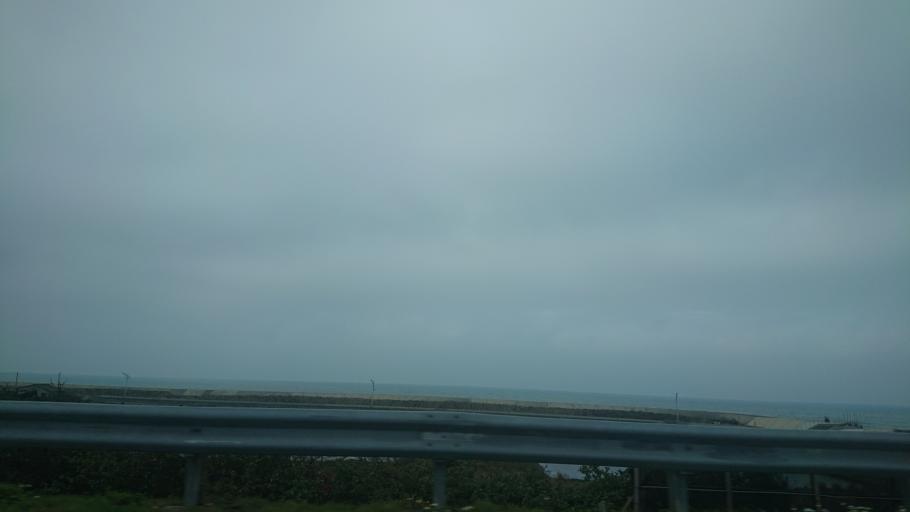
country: TW
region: Taiwan
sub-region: Miaoli
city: Miaoli
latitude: 24.5191
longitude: 120.6870
